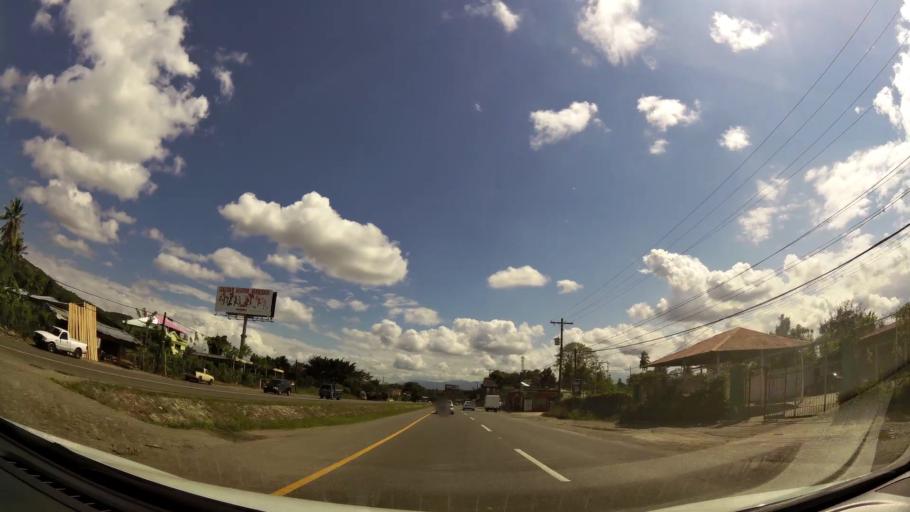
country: DO
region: La Vega
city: Rio Verde Arriba
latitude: 19.3068
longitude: -70.5848
